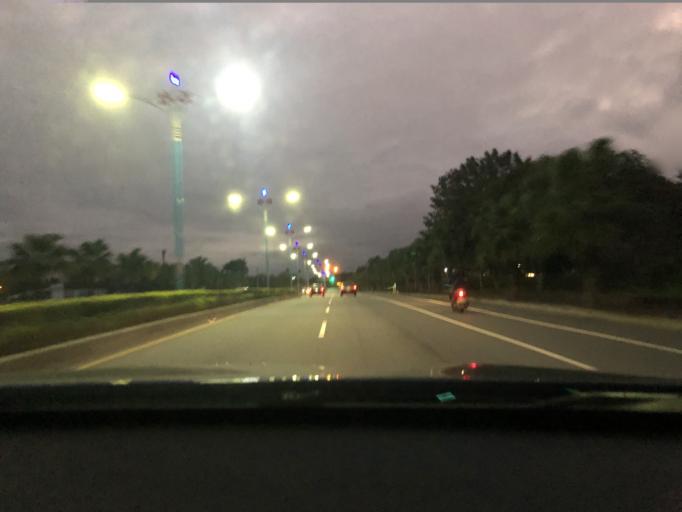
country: TW
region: Taiwan
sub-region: Hualien
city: Hualian
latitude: 23.9555
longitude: 121.5611
